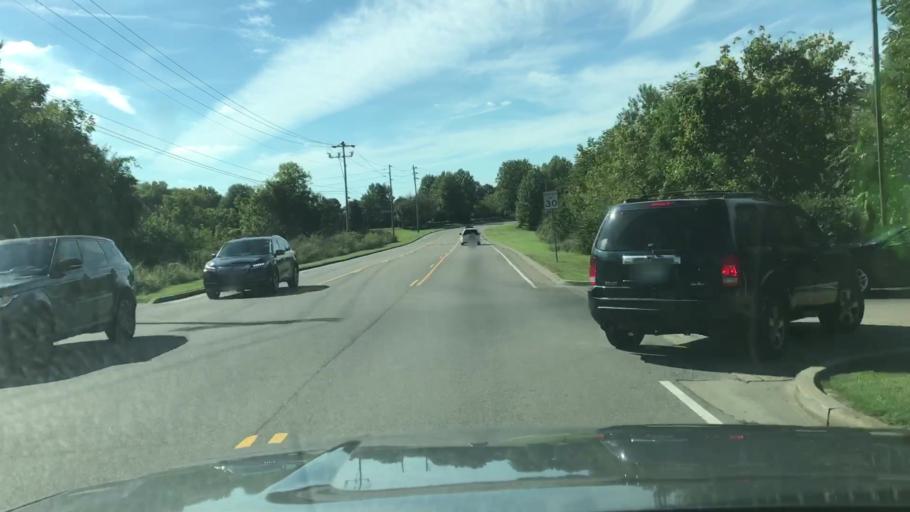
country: US
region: Tennessee
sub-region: Williamson County
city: Franklin
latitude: 35.9523
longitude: -86.8189
